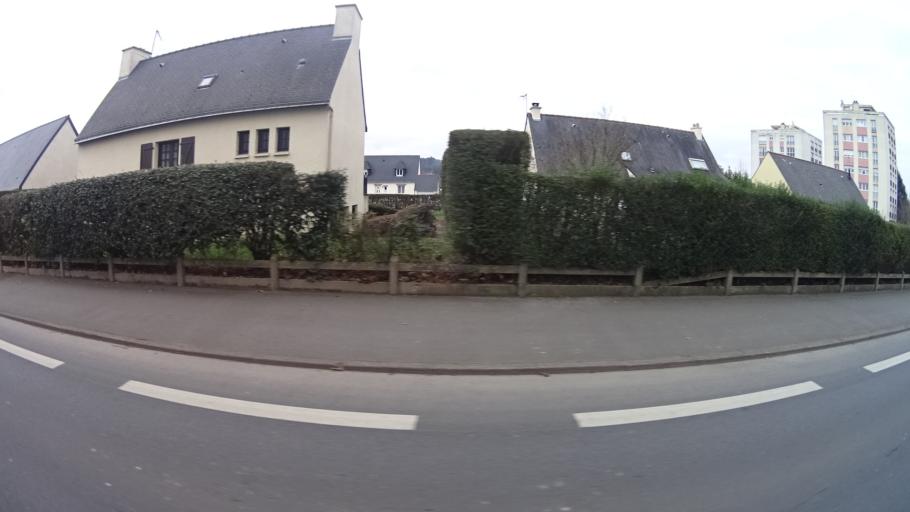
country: FR
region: Brittany
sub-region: Departement d'Ille-et-Vilaine
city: Redon
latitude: 47.6630
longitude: -2.0712
